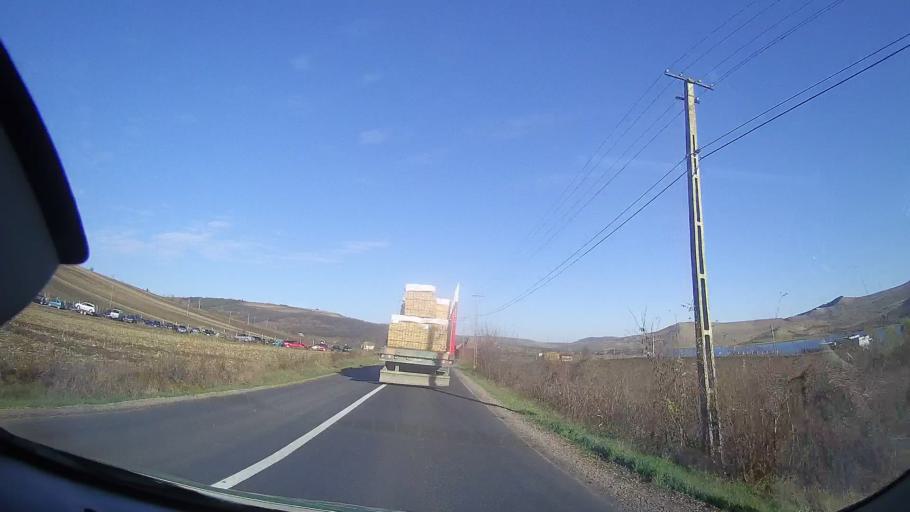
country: RO
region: Mures
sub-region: Comuna Zau De Campie
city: Zau de Campie
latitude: 46.6311
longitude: 24.1322
